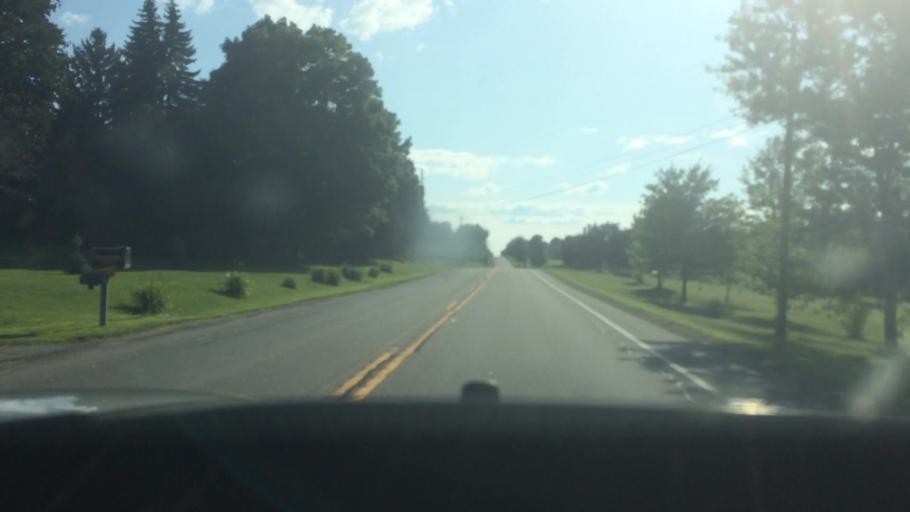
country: US
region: New York
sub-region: Franklin County
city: Malone
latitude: 44.7953
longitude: -74.4634
